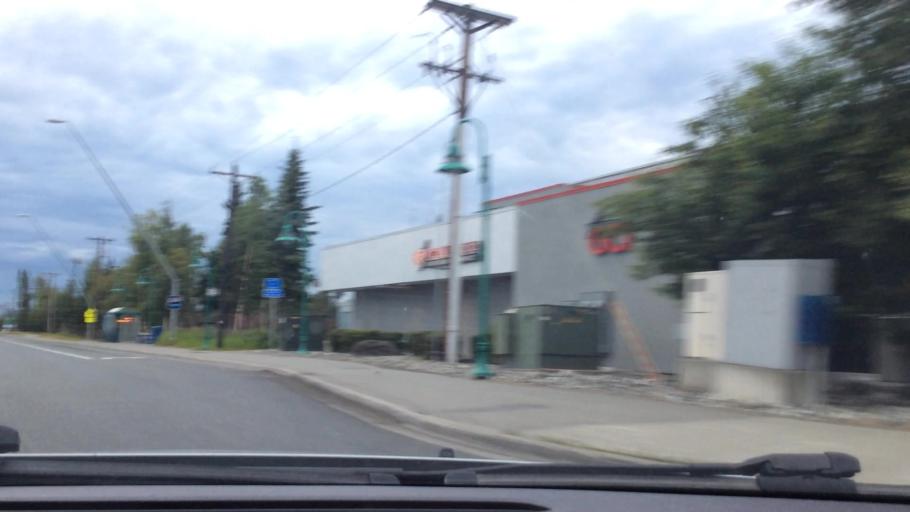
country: US
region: Alaska
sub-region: Anchorage Municipality
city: Elmendorf Air Force Base
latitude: 61.2098
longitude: -149.7337
